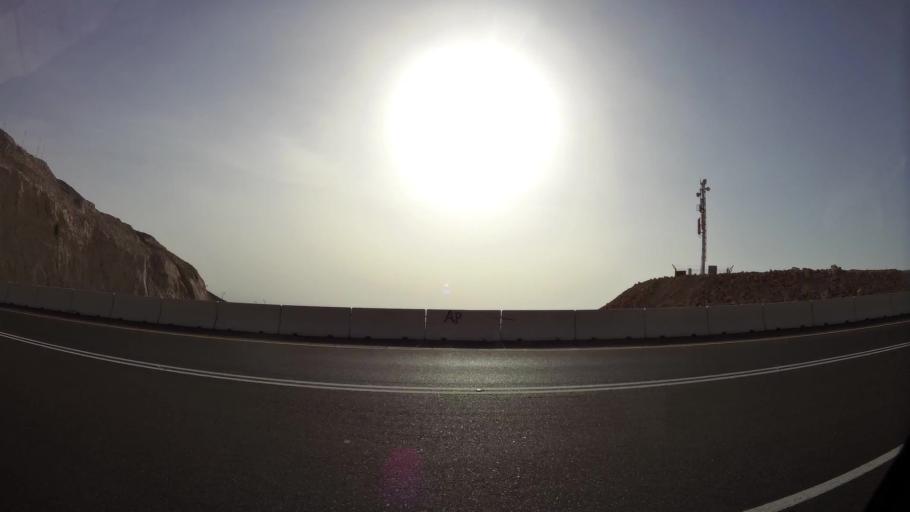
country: AE
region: Abu Dhabi
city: Al Ain
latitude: 24.0873
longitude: 55.7658
